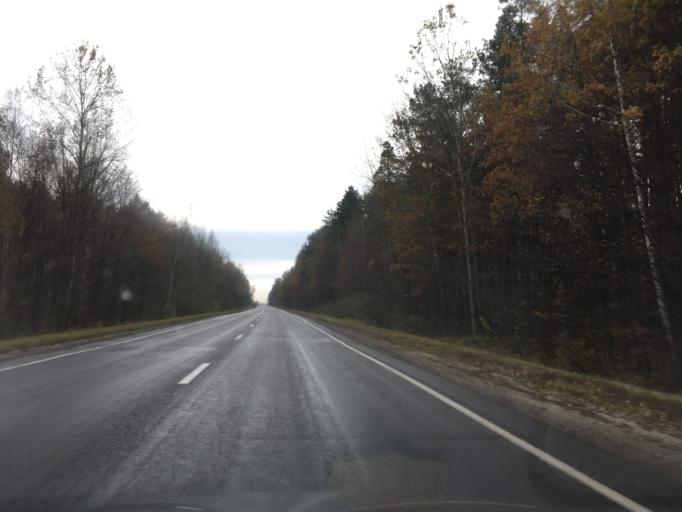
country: BY
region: Gomel
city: Kastsyukowka
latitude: 52.4252
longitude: 30.8282
